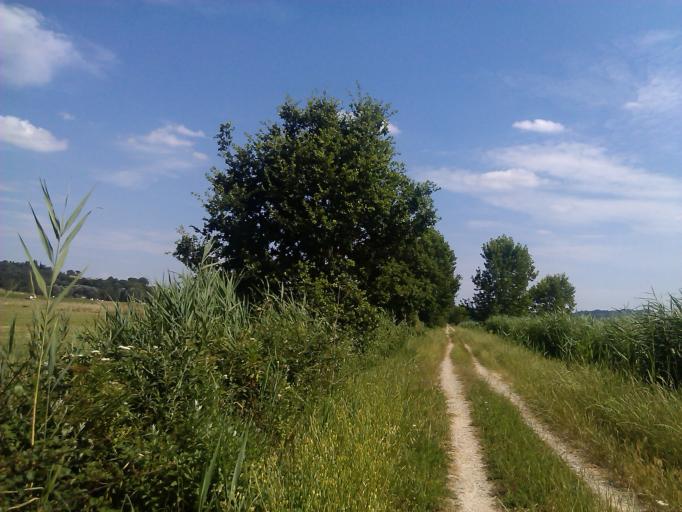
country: IT
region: Tuscany
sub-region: Provincia di Siena
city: Chiusi
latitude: 43.0671
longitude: 11.9295
